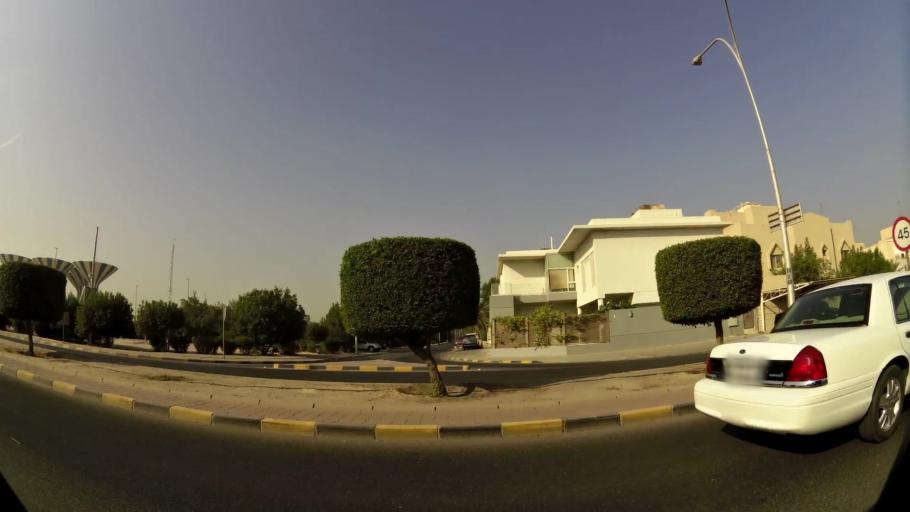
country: KW
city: Bayan
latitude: 29.3115
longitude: 48.0413
